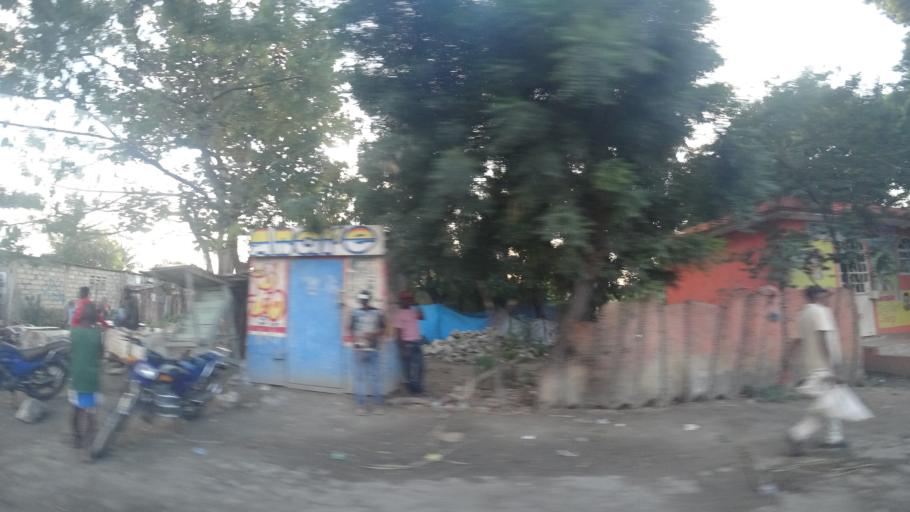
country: HT
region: Ouest
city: Delmas 73
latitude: 18.6063
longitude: -72.3201
